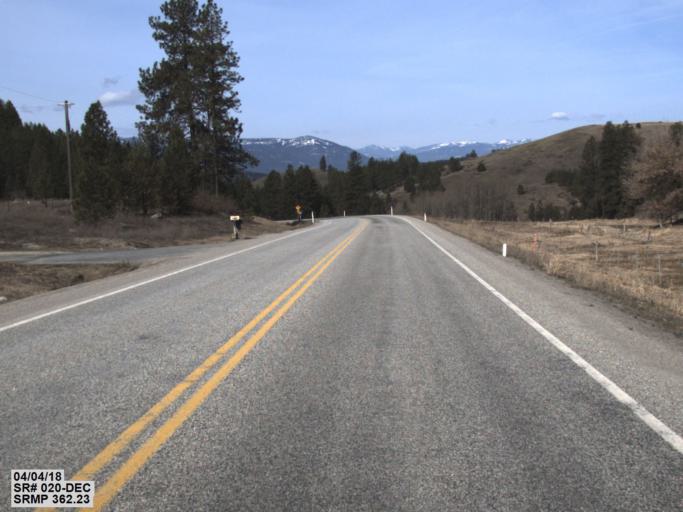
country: US
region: Washington
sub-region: Stevens County
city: Colville
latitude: 48.5157
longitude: -117.7640
